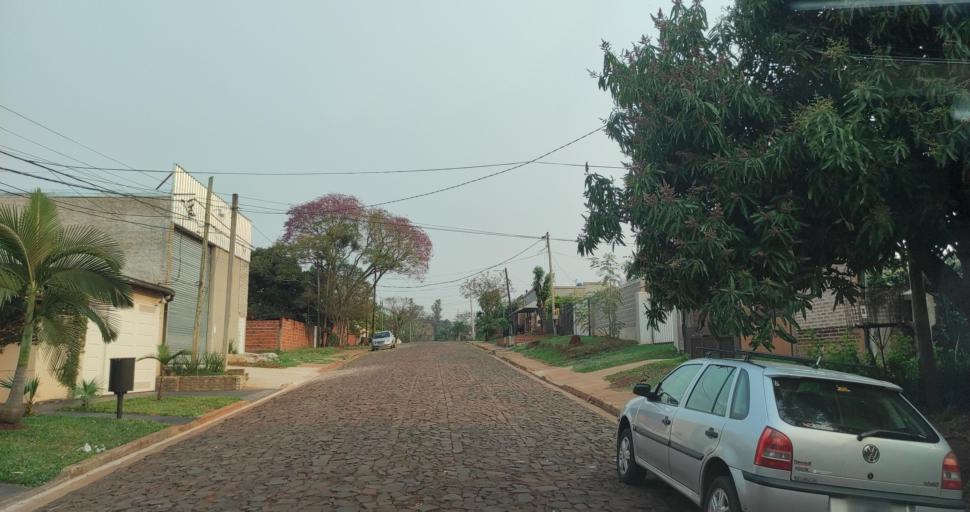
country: AR
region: Misiones
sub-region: Departamento de Capital
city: Posadas
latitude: -27.3970
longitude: -55.9264
